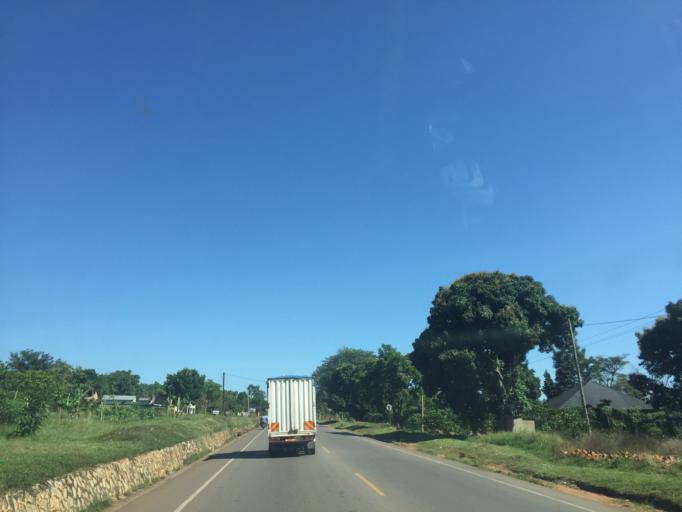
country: UG
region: Central Region
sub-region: Luwero District
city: Luwero
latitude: 0.8068
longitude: 32.5058
